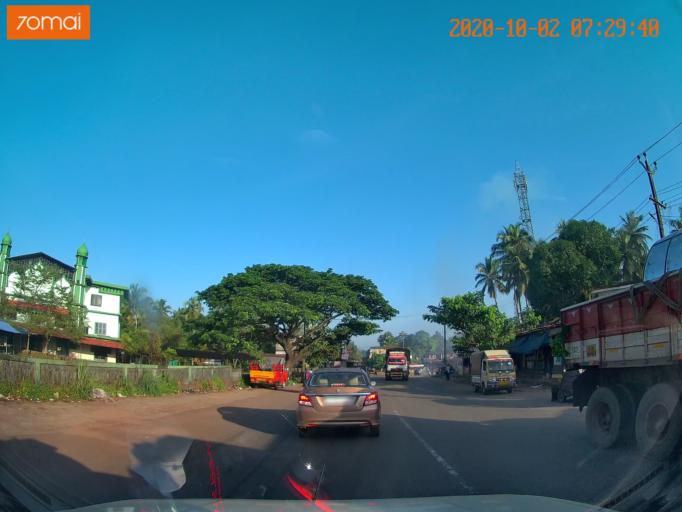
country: IN
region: Kerala
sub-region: Malappuram
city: Pariyapuram
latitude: 11.0354
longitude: 75.9378
